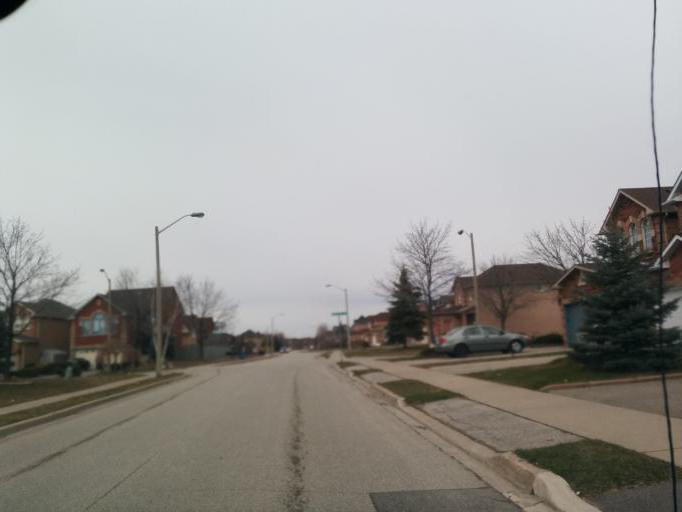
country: CA
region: Ontario
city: Brampton
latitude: 43.7262
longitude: -79.8200
